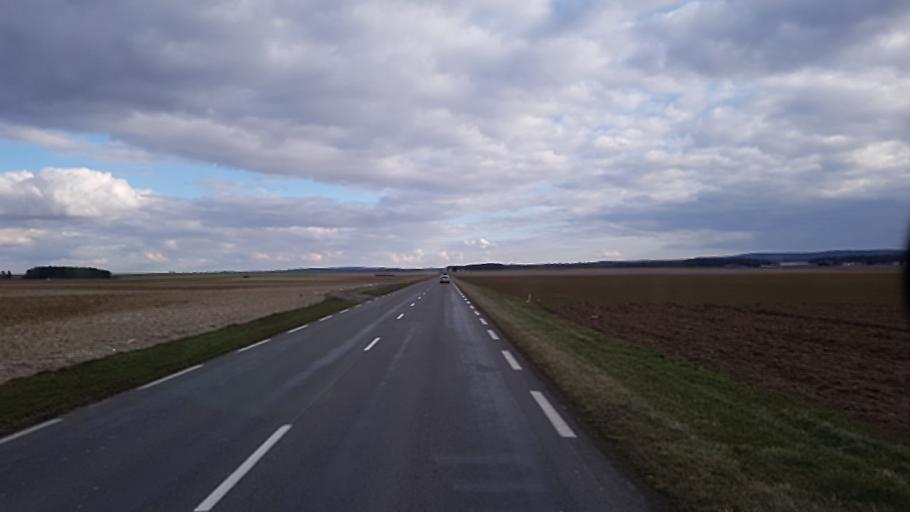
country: FR
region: Picardie
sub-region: Departement de l'Aisne
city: Saint-Erme-Outre-et-Ramecourt
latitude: 49.4467
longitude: 3.8440
